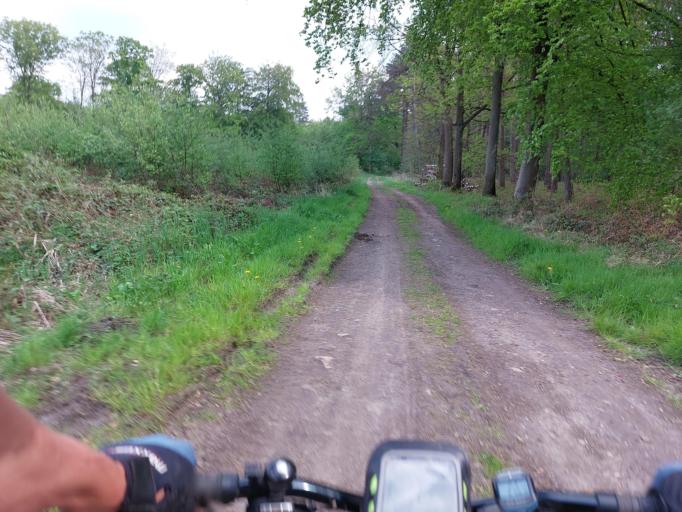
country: BE
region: Wallonia
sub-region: Province du Hainaut
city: Jurbise
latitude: 50.4998
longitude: 3.8981
